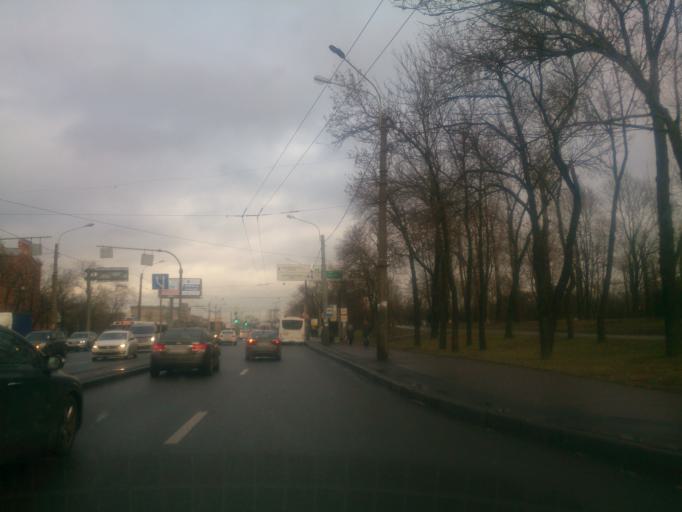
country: RU
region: St.-Petersburg
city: Dachnoye
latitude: 59.8589
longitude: 30.2539
